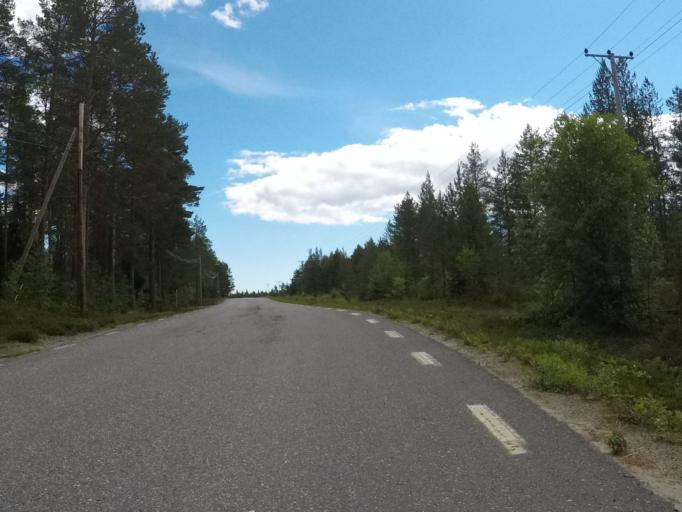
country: SE
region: Vaesterbotten
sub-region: Robertsfors Kommun
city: Robertsfors
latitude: 63.9922
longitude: 20.8205
